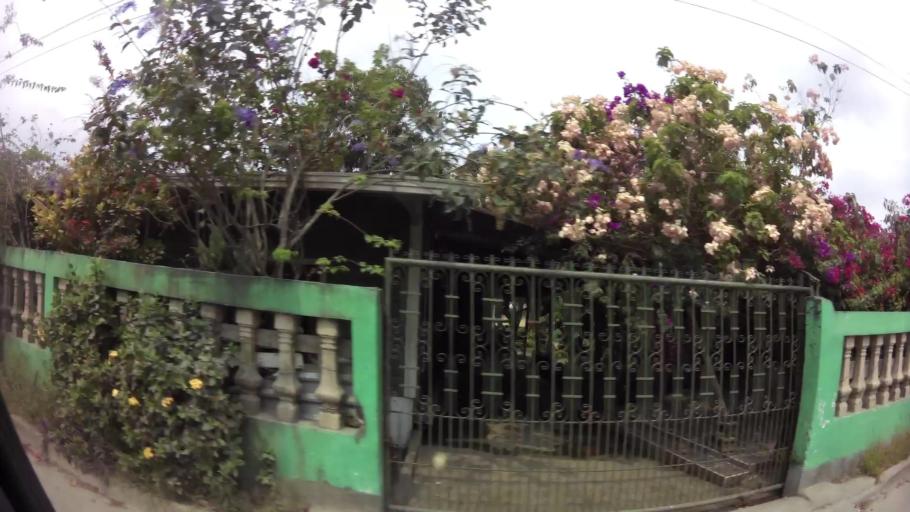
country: HN
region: Atlantida
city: Tela
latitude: 15.7708
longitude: -87.4820
